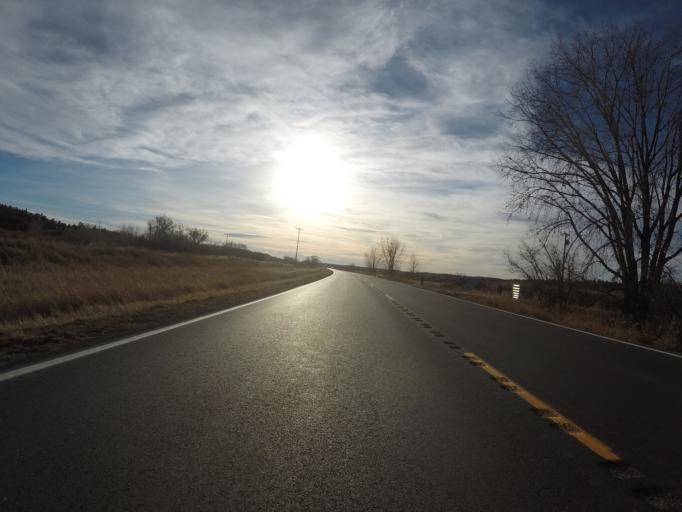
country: US
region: Montana
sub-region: Musselshell County
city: Roundup
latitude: 46.3576
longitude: -108.6674
